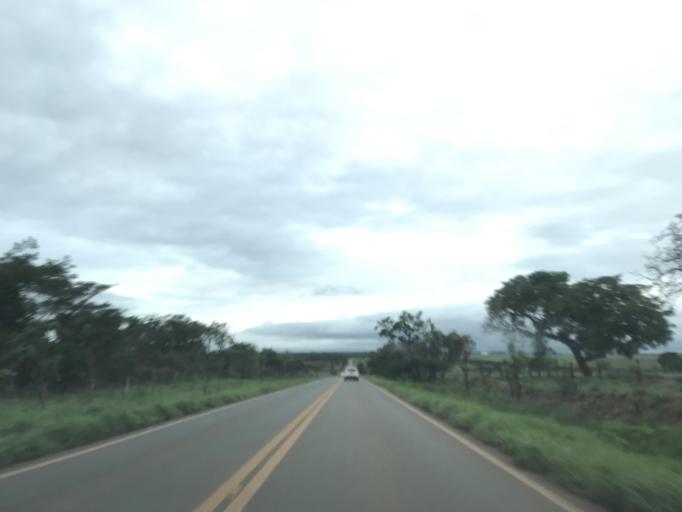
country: BR
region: Goias
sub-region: Luziania
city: Luziania
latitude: -16.2849
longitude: -48.0005
